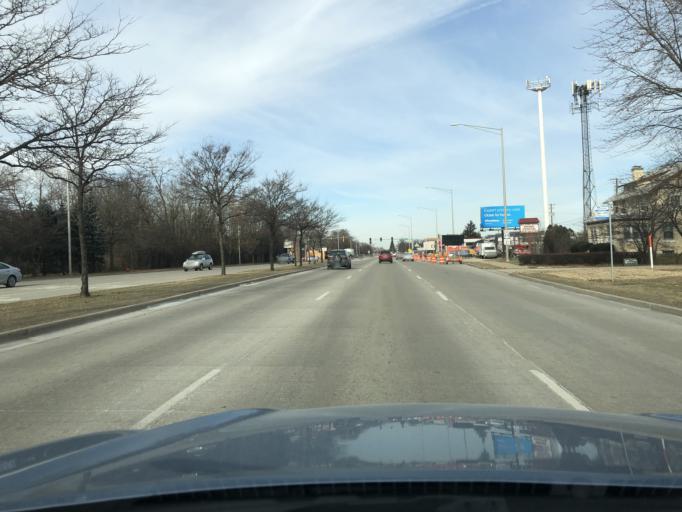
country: US
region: Illinois
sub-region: Cook County
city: Wheeling
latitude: 42.1547
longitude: -87.9153
